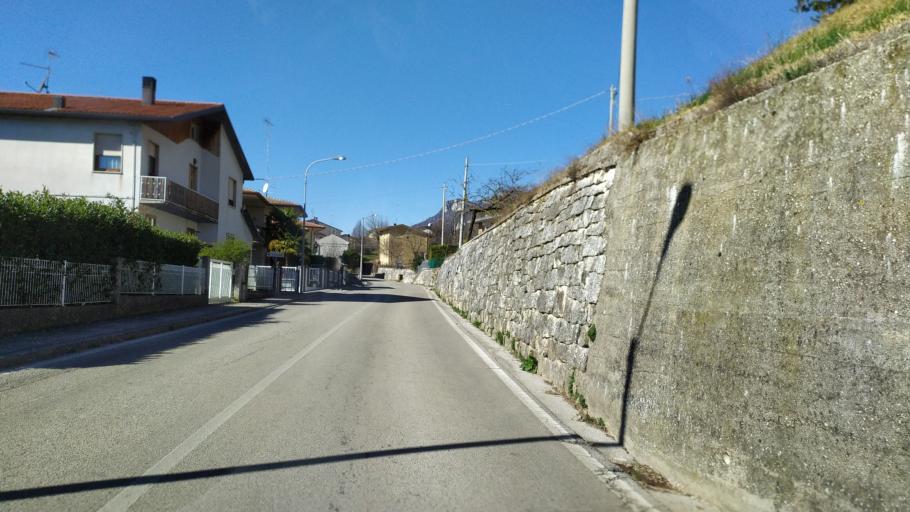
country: IT
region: Veneto
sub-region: Provincia di Vicenza
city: Chiuppano
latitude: 45.7673
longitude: 11.4698
